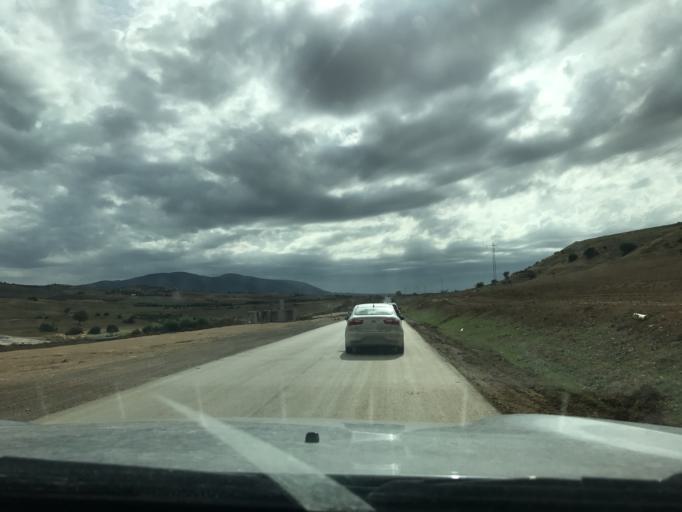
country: TN
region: Silyanah
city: Bu `Aradah
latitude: 36.1805
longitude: 9.6656
